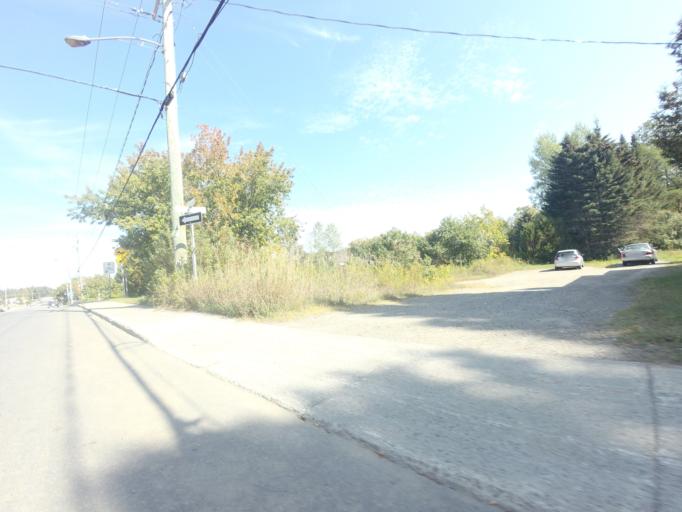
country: CA
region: Quebec
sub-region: Laurentides
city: Sainte-Agathe-des-Monts
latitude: 46.0496
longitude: -74.2800
